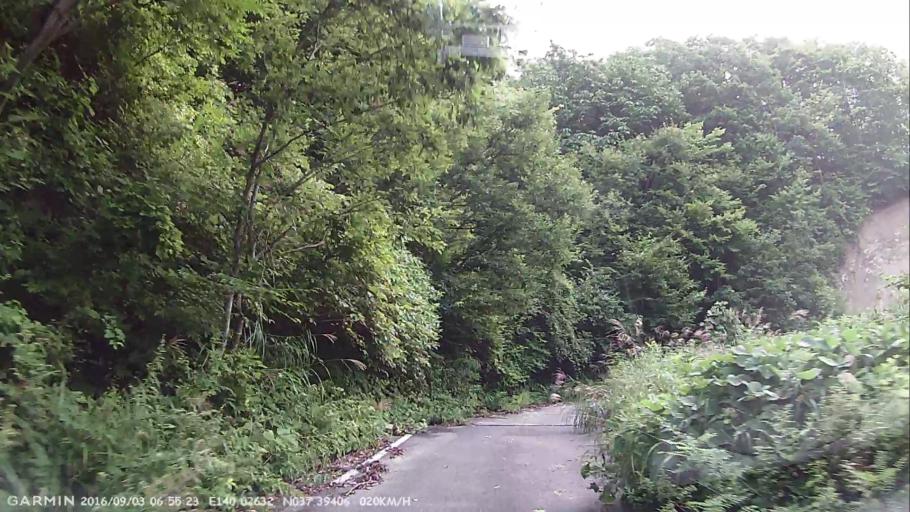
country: JP
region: Fukushima
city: Inawashiro
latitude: 37.3941
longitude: 140.0263
